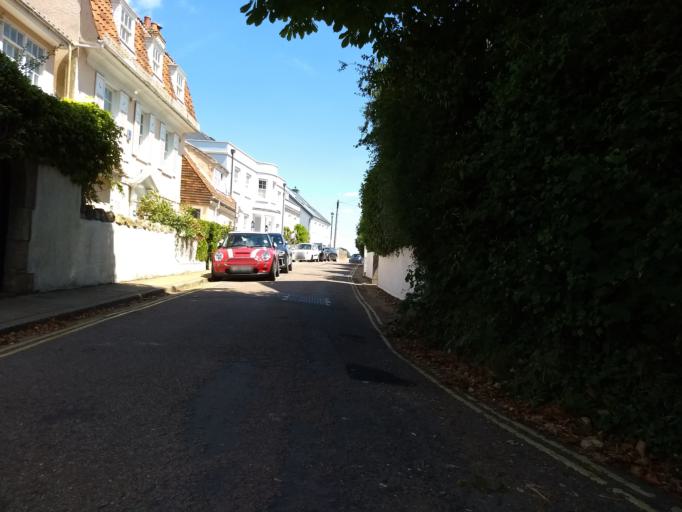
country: GB
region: England
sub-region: Isle of Wight
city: Yarmouth
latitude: 50.7064
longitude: -1.4959
